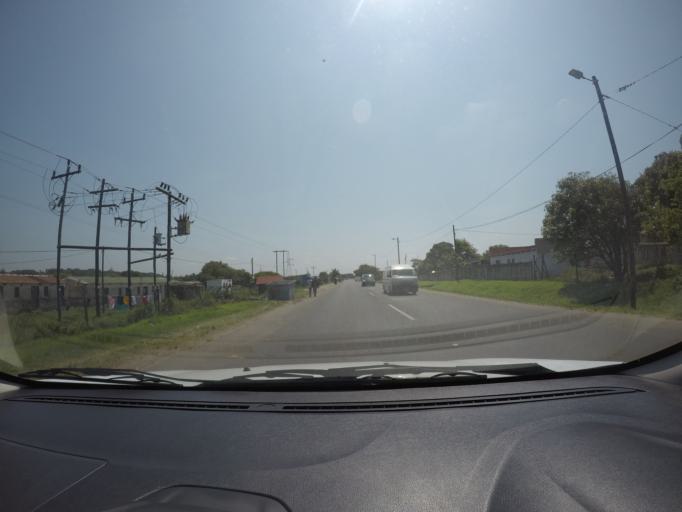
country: ZA
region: KwaZulu-Natal
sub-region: uThungulu District Municipality
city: eSikhawini
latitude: -28.8597
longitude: 31.9194
